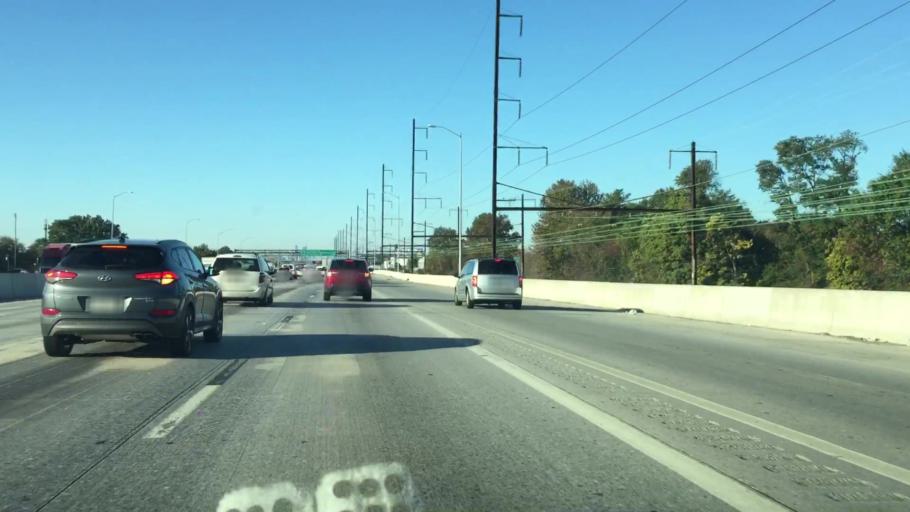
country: US
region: New Jersey
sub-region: Burlington County
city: Palmyra
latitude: 40.0196
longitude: -75.0436
